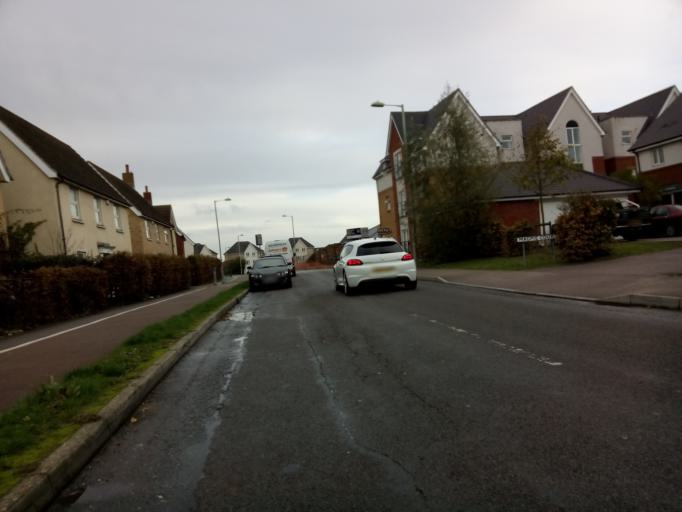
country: GB
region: England
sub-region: Suffolk
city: Stowmarket
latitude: 52.1880
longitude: 1.0138
